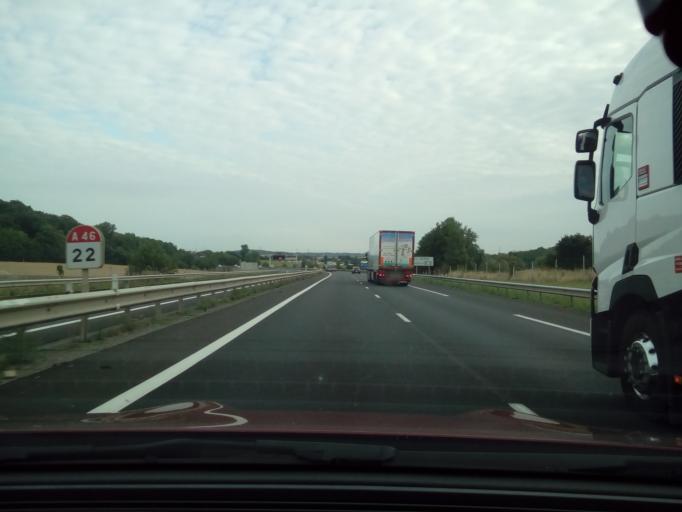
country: FR
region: Rhone-Alpes
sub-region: Departement du Rhone
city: Rillieux-la-Pape
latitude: 45.8361
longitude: 4.9173
